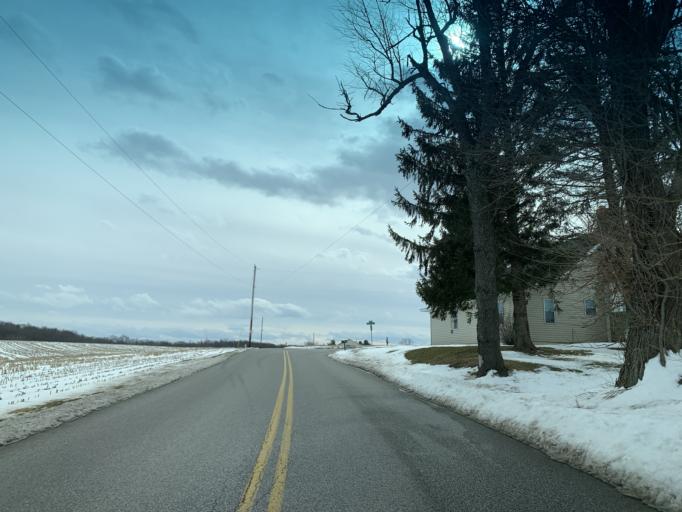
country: US
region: Pennsylvania
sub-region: York County
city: Shrewsbury
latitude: 39.7776
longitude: -76.6474
